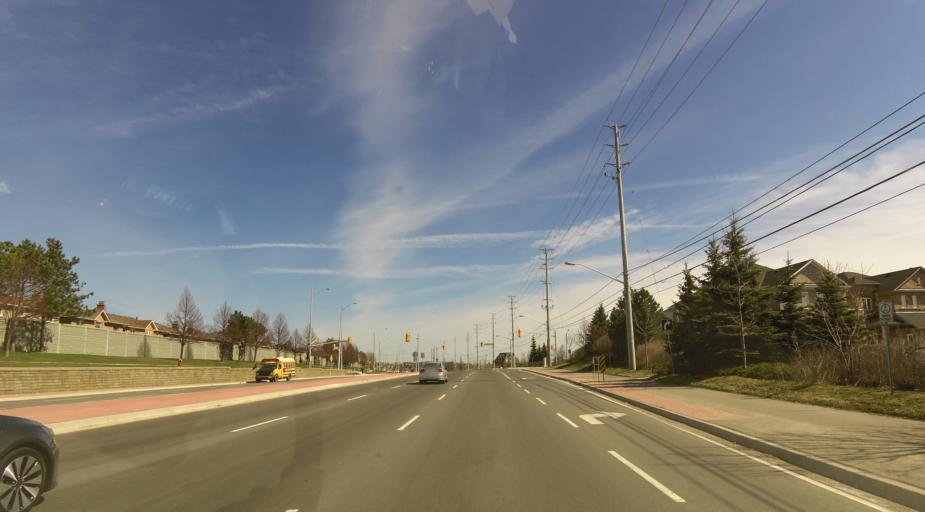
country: CA
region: Ontario
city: Brampton
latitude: 43.6442
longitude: -79.7511
